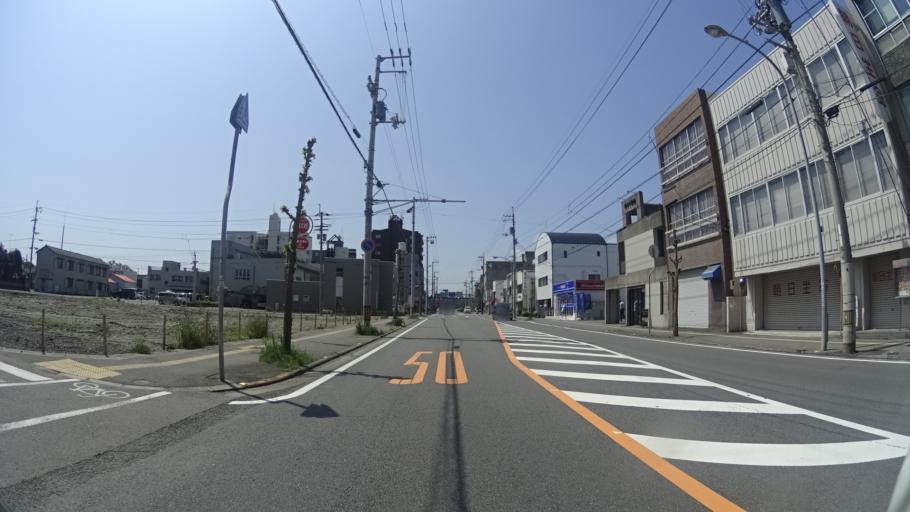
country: JP
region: Tokushima
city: Narutocho-mitsuishi
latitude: 34.1760
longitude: 134.6087
